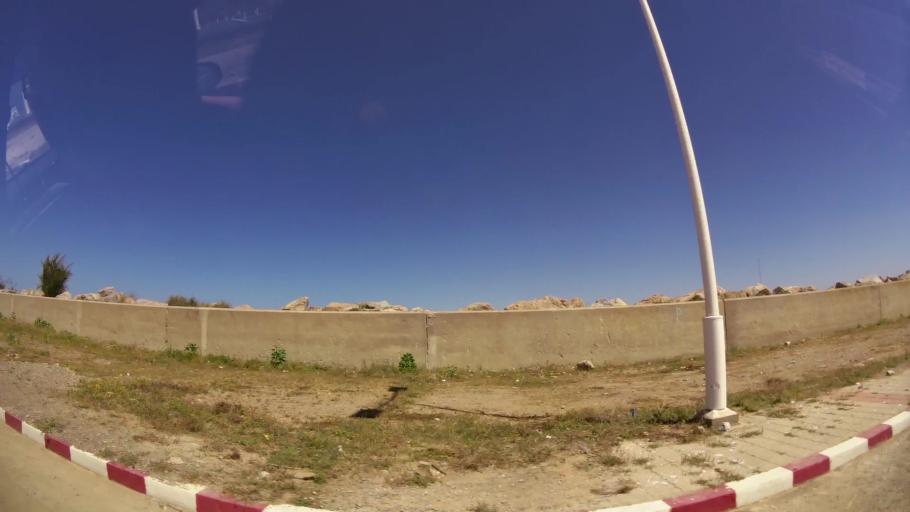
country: MA
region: Oriental
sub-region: Berkane-Taourirt
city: Madagh
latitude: 35.1428
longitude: -2.4219
